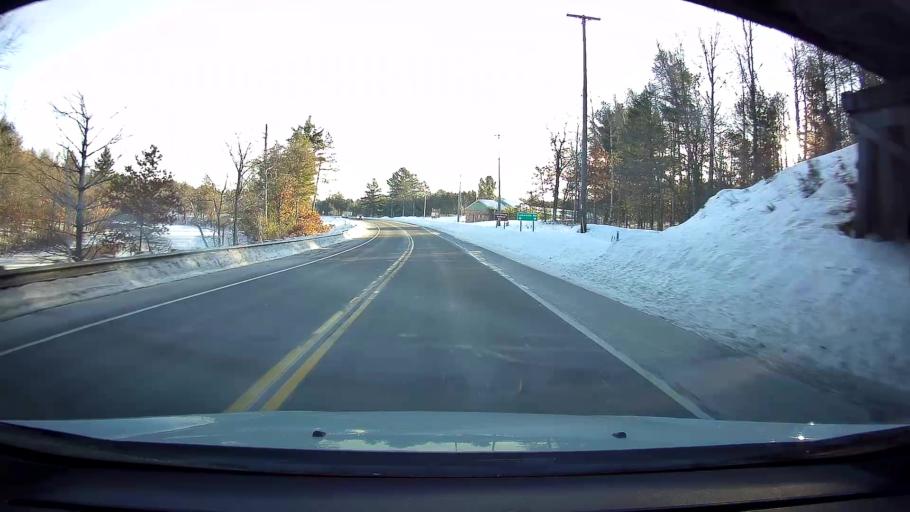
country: US
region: Wisconsin
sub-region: Washburn County
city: Spooner
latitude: 45.9052
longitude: -91.8182
